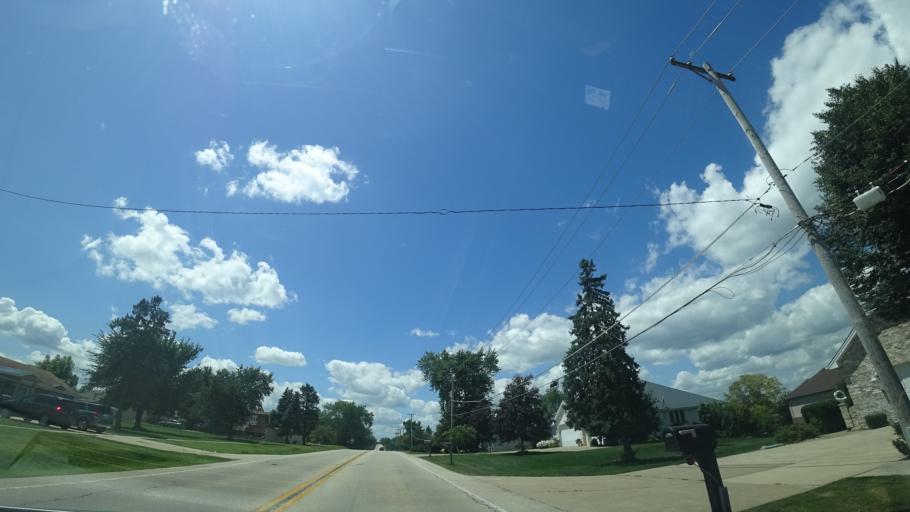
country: US
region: Illinois
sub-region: Cook County
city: Orland Hills
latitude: 41.5863
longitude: -87.8867
